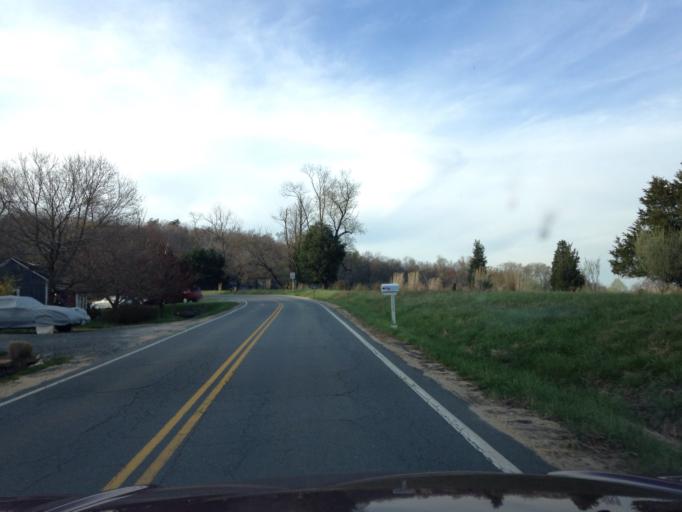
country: US
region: Maryland
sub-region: Frederick County
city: Point of Rocks
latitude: 39.2363
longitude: -77.5570
